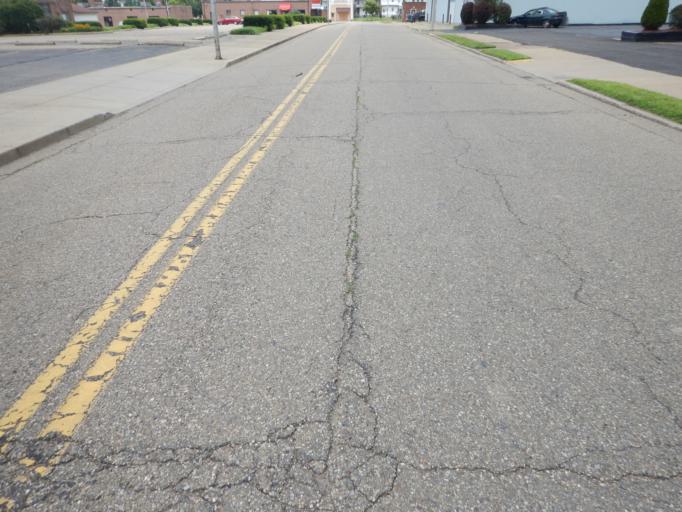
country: US
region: Ohio
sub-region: Muskingum County
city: Zanesville
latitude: 39.9388
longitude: -82.0029
